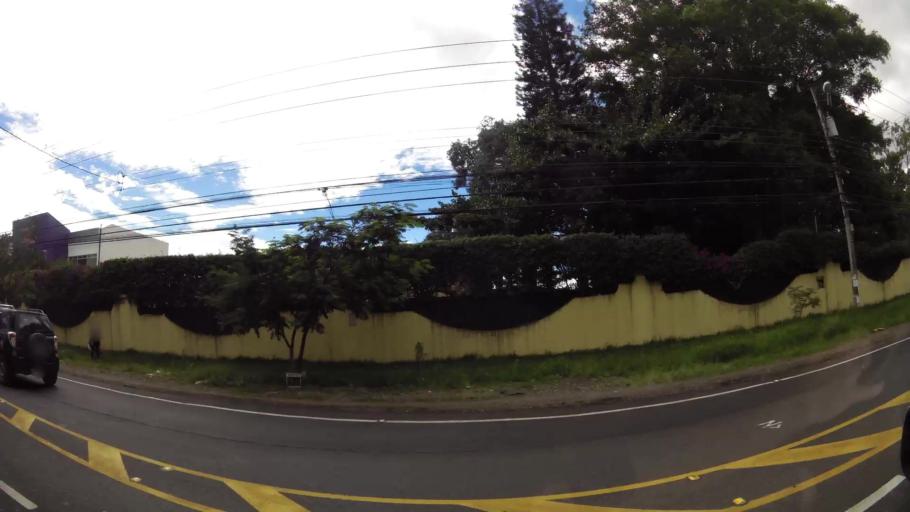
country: CR
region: Cartago
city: San Diego
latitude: 9.9109
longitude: -84.0136
